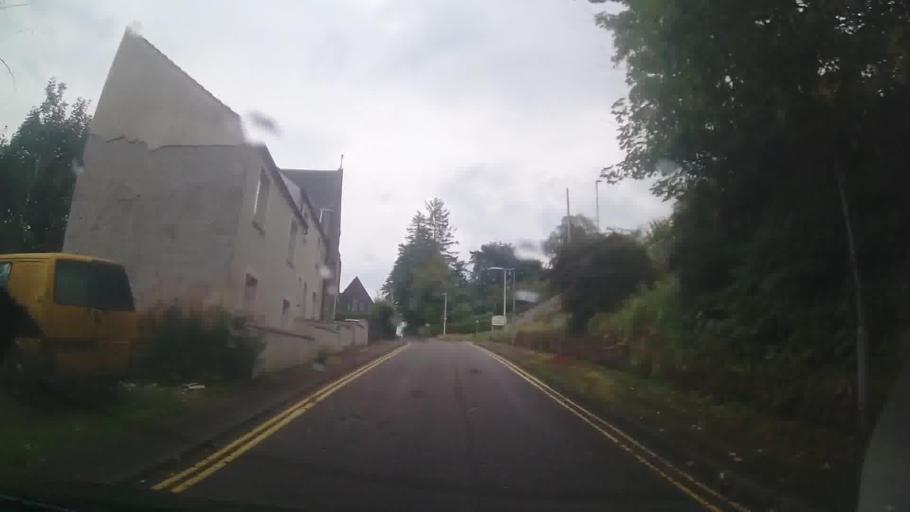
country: GB
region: Scotland
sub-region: Highland
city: Fort William
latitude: 56.8161
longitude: -5.1125
